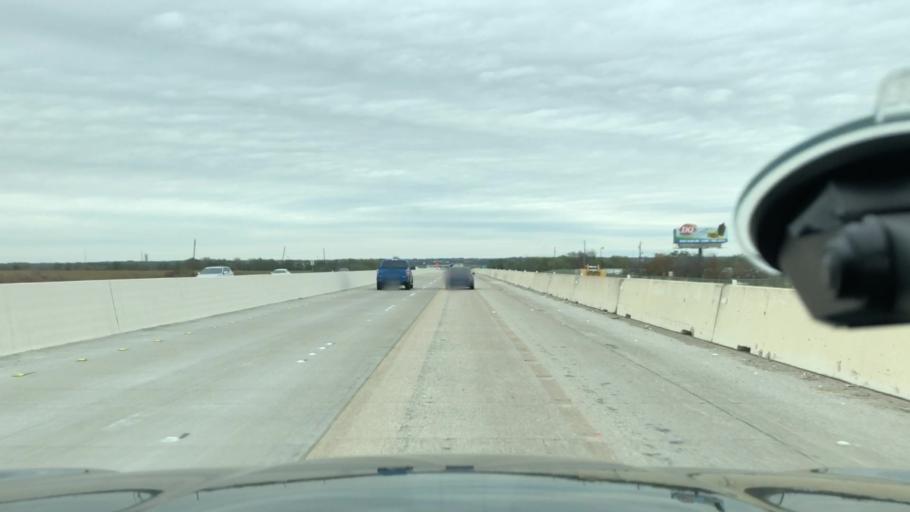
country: US
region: Texas
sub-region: Ellis County
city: Red Oak
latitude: 32.4839
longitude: -96.8304
